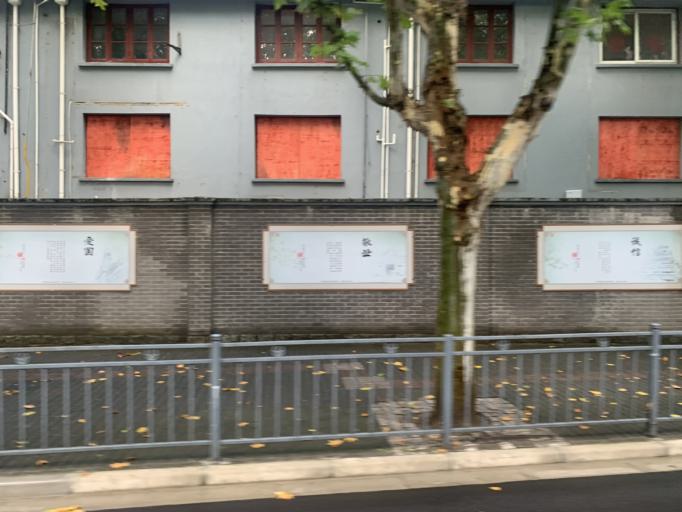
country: CN
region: Shanghai Shi
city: Luwan
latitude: 31.2131
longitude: 121.4736
